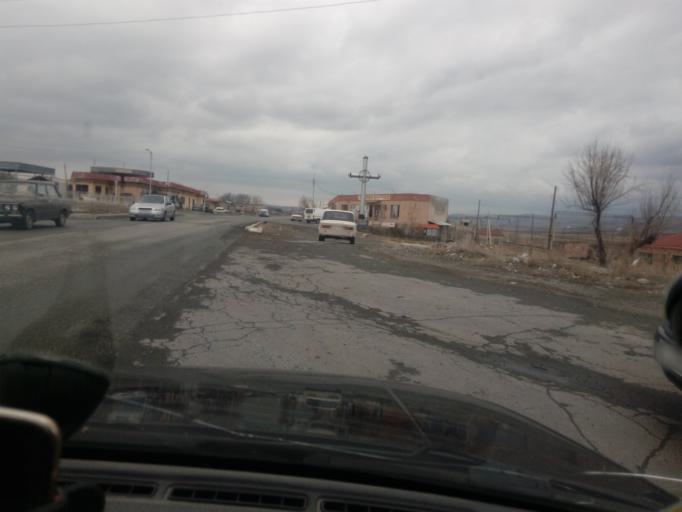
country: AM
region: Aragatsotn
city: Arteni
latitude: 40.2785
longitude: 43.8061
